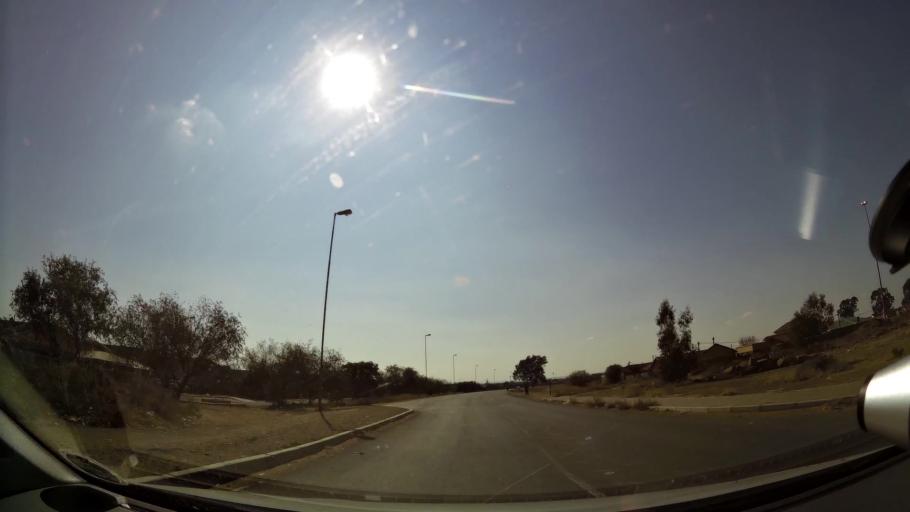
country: ZA
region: Orange Free State
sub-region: Mangaung Metropolitan Municipality
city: Bloemfontein
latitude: -29.1563
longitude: 26.2566
